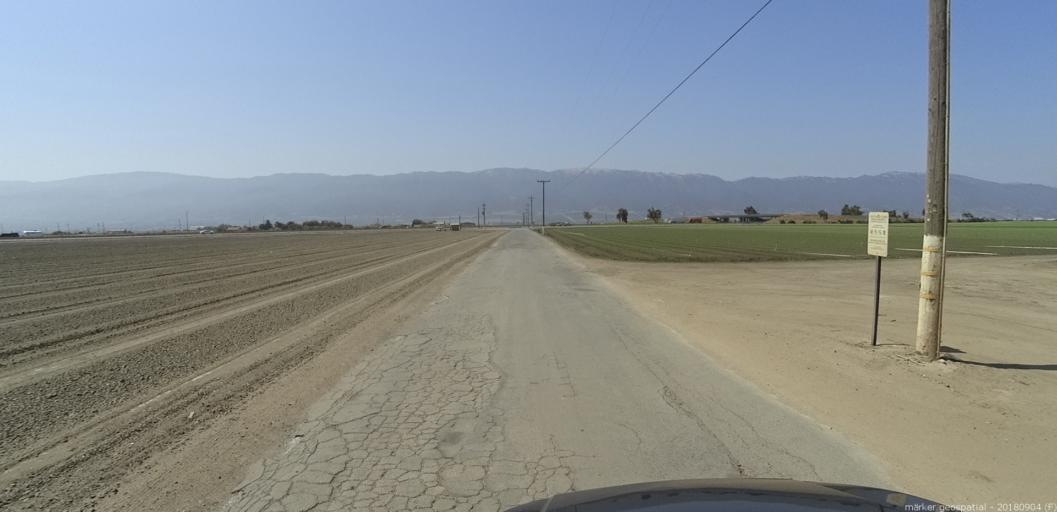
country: US
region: California
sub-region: Monterey County
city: Gonzales
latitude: 36.5247
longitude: -121.4588
